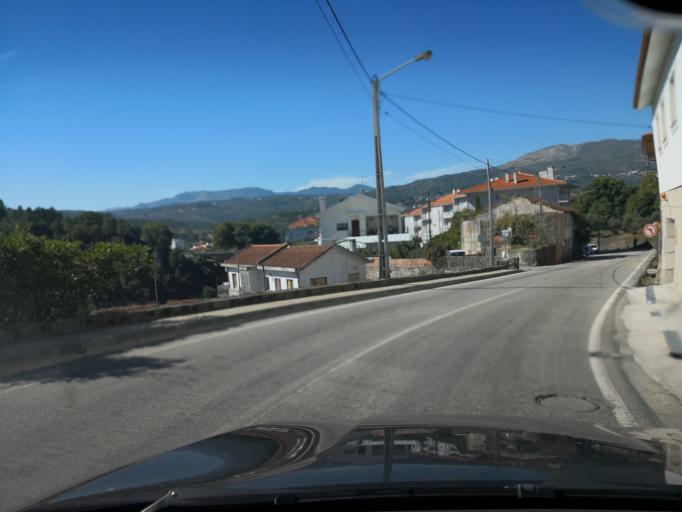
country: PT
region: Vila Real
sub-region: Vila Real
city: Vila Real
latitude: 41.2953
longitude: -7.7515
